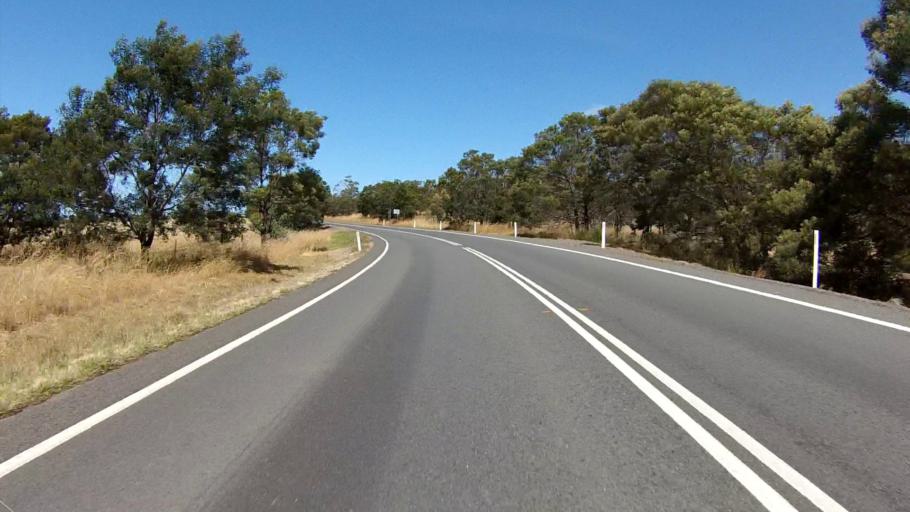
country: AU
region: Tasmania
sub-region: Break O'Day
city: St Helens
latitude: -42.0764
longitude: 148.0673
